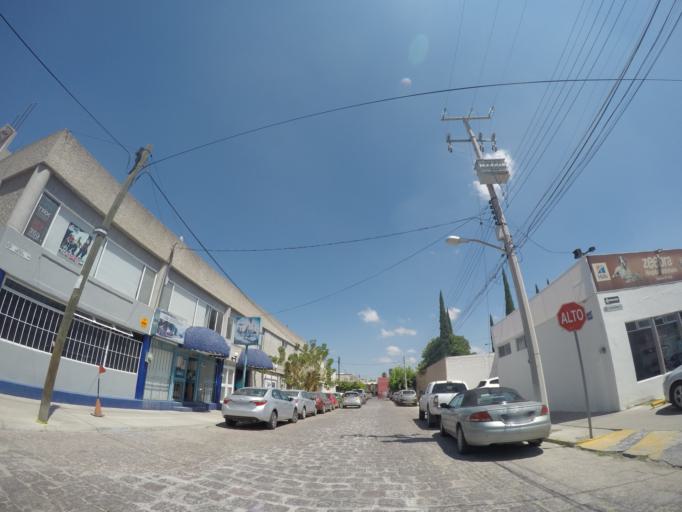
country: MX
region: San Luis Potosi
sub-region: San Luis Potosi
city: San Luis Potosi
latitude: 22.1475
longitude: -101.0109
